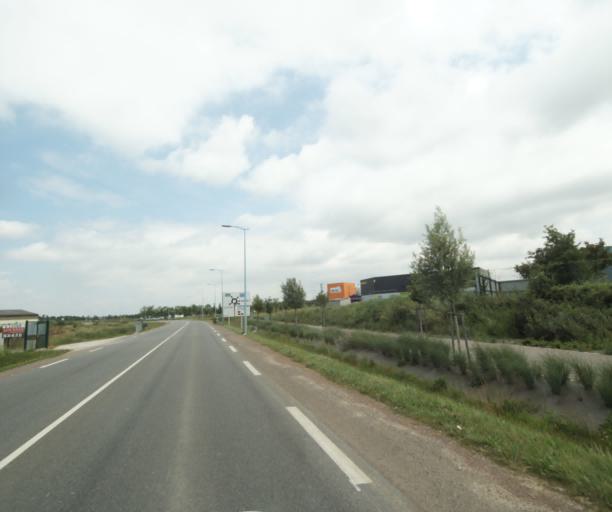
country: FR
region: Midi-Pyrenees
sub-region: Departement du Tarn-et-Garonne
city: Montauban
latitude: 44.0442
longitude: 1.3864
